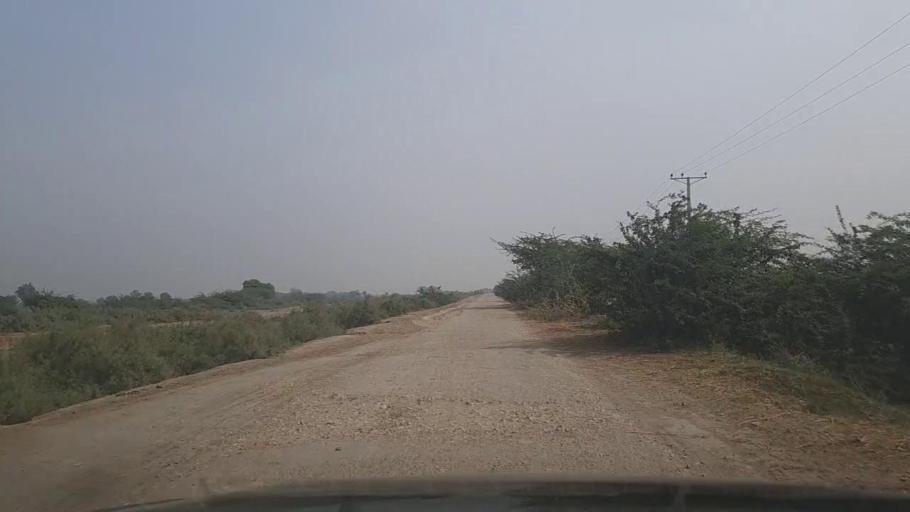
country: PK
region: Sindh
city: Mirpur Sakro
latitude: 24.4791
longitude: 67.6518
